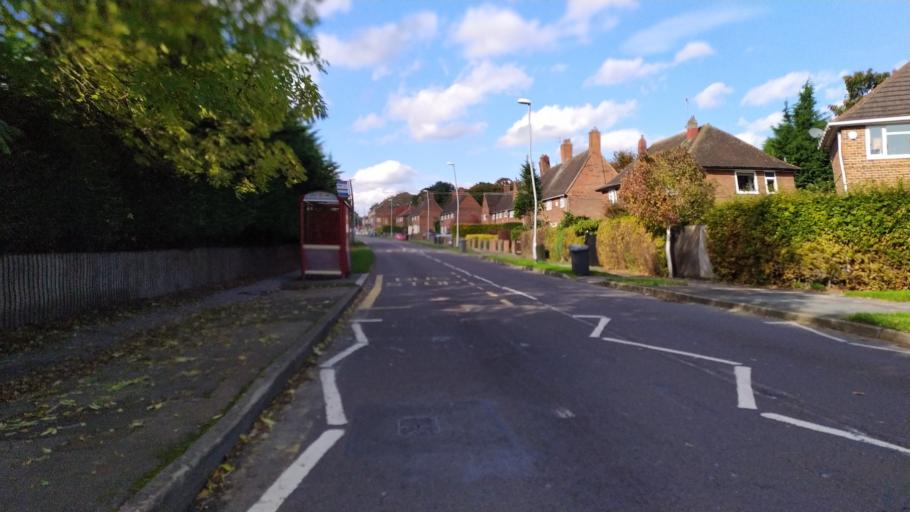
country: GB
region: England
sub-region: City and Borough of Leeds
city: Horsforth
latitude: 53.8200
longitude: -1.5939
